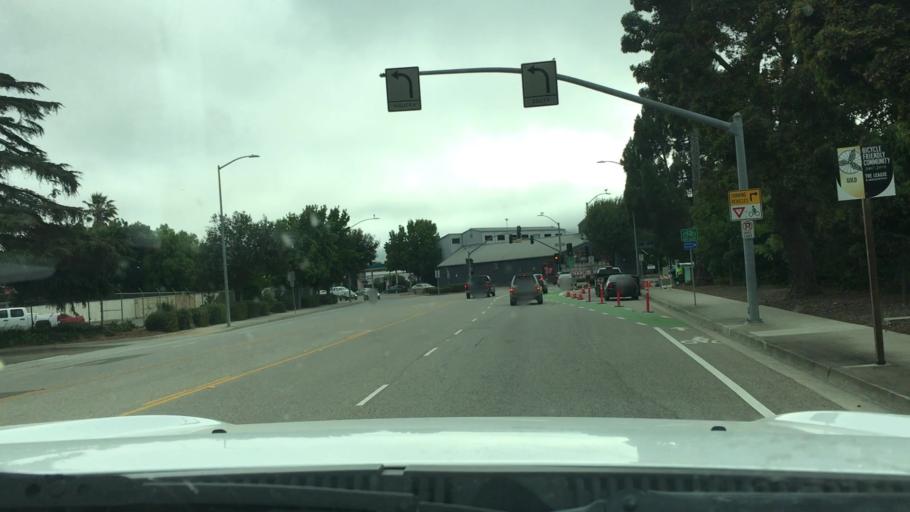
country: US
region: California
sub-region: San Luis Obispo County
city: San Luis Obispo
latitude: 35.2676
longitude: -120.6714
